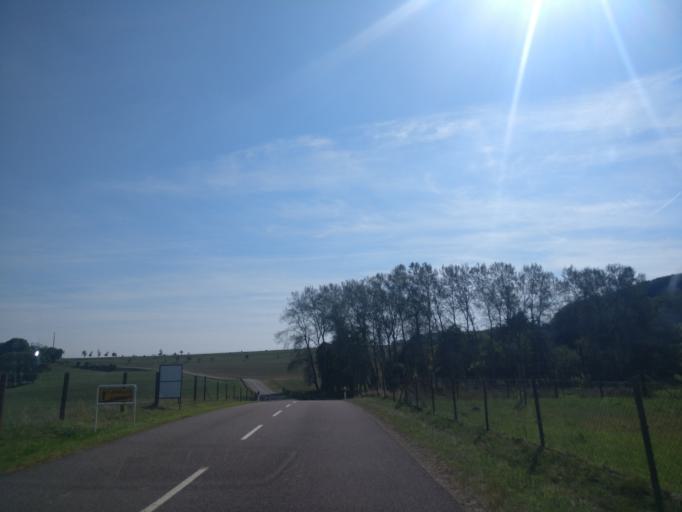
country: LU
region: Grevenmacher
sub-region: Canton de Grevenmacher
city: Flaxweiler
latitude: 49.6715
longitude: 6.3301
